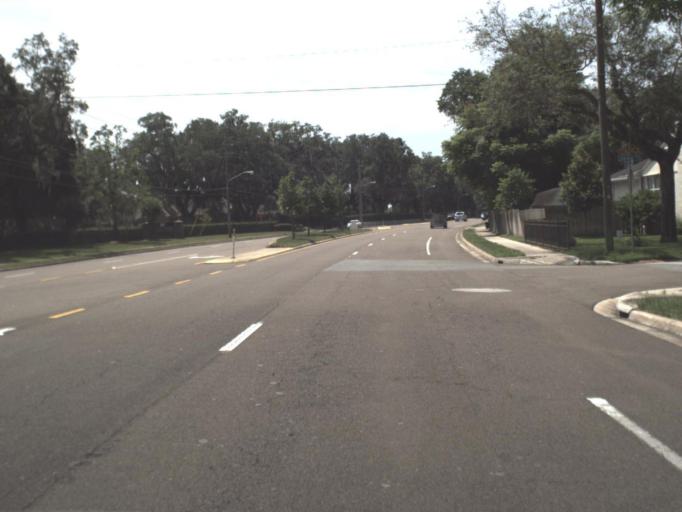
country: US
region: Florida
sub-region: Duval County
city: Jacksonville
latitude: 30.2712
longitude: -81.6488
